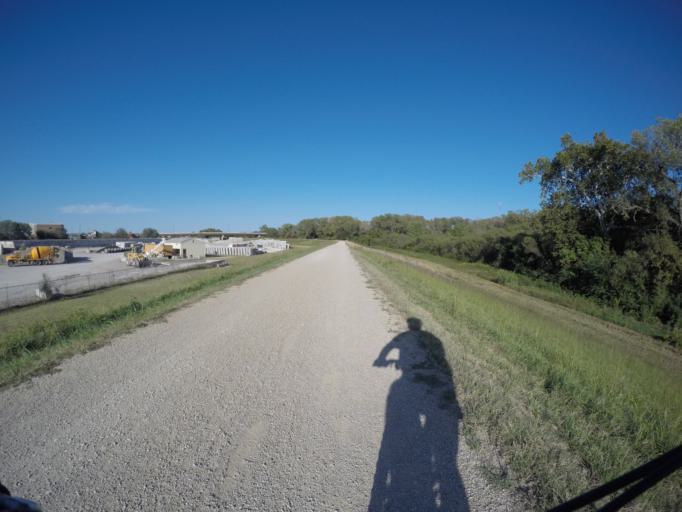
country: US
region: Kansas
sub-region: Riley County
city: Manhattan
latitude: 39.1724
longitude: -96.5590
